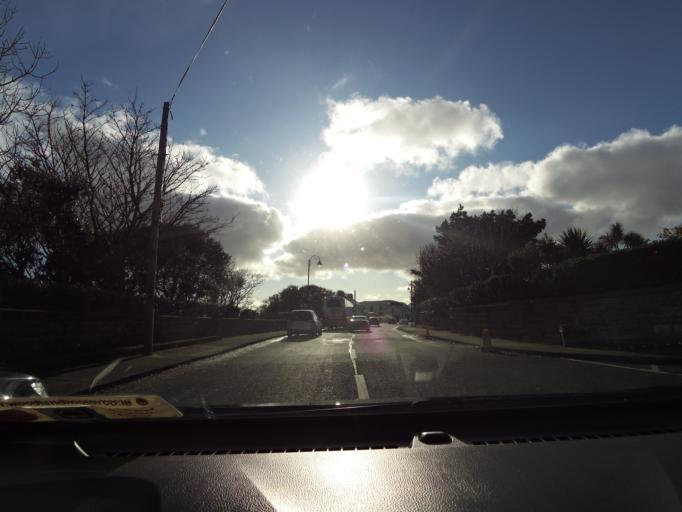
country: IE
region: Connaught
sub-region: Maigh Eo
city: Belmullet
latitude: 53.9319
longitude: -9.9237
